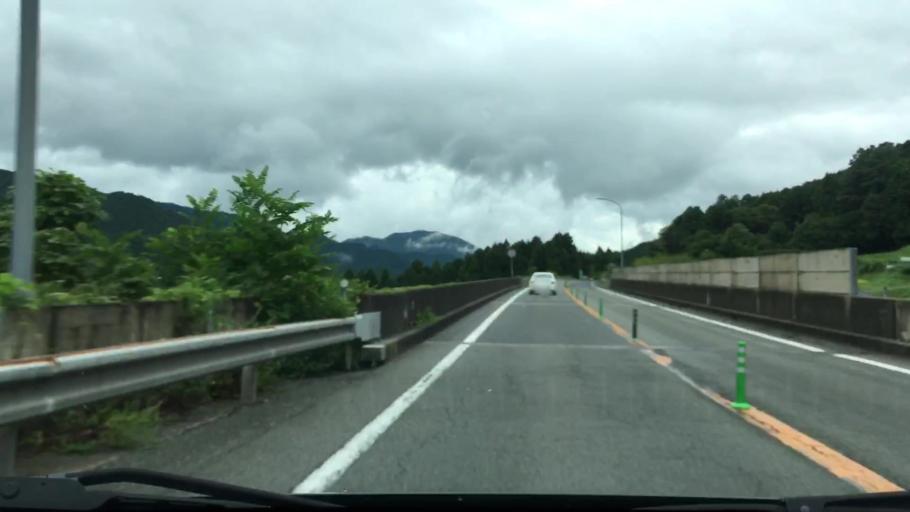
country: JP
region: Hyogo
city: Nishiwaki
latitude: 35.0999
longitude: 134.7771
